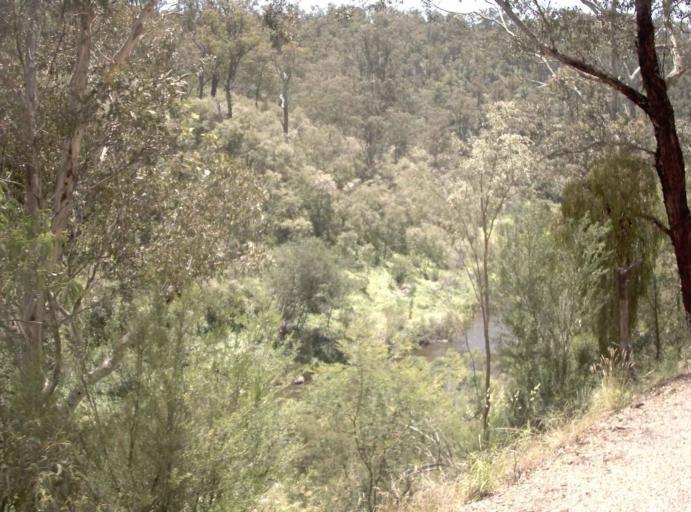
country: AU
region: Victoria
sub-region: East Gippsland
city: Bairnsdale
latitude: -37.4577
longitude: 147.8295
